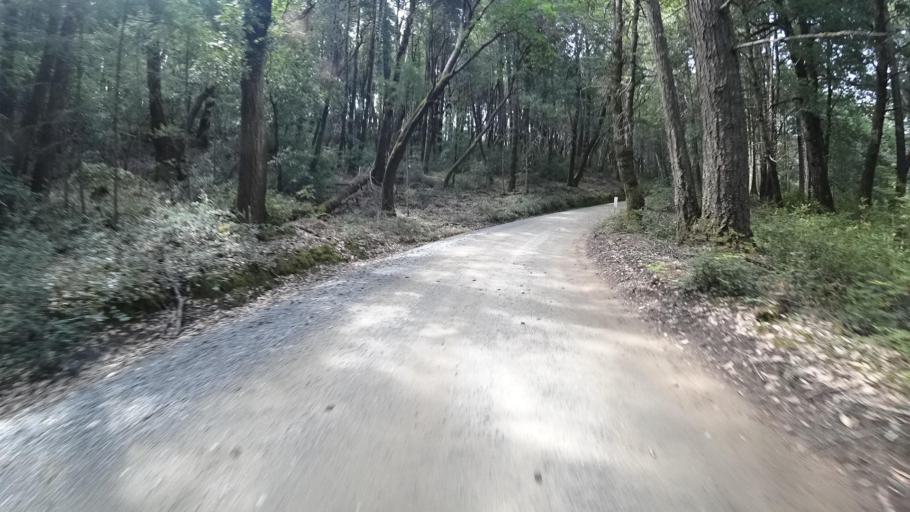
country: US
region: California
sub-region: Humboldt County
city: Redway
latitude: 40.0412
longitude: -123.8483
